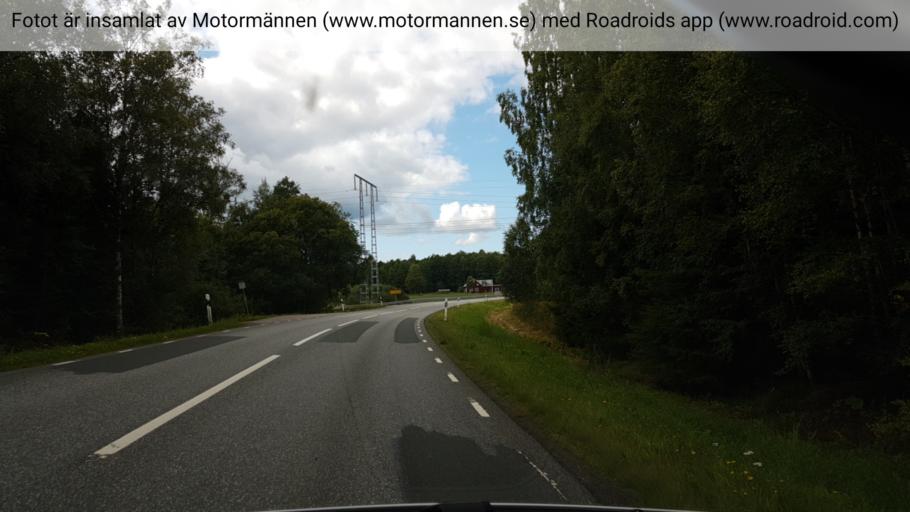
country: SE
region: Joenkoeping
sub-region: Aneby Kommun
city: Aneby
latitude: 57.9750
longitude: 14.7762
